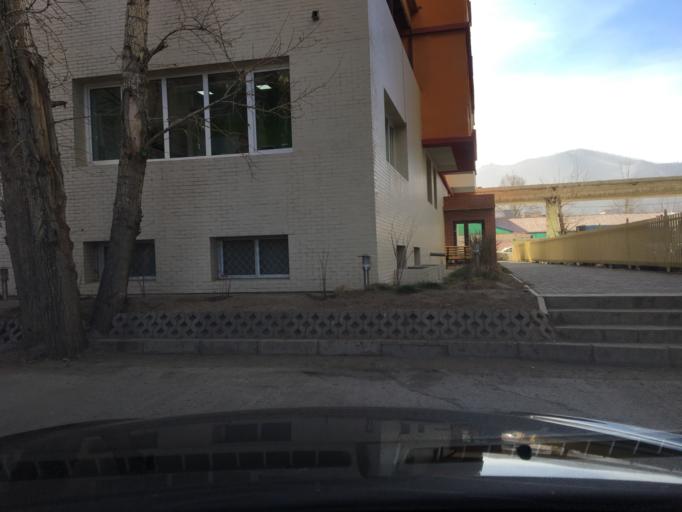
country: MN
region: Ulaanbaatar
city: Ulaanbaatar
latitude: 47.8963
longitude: 106.8947
